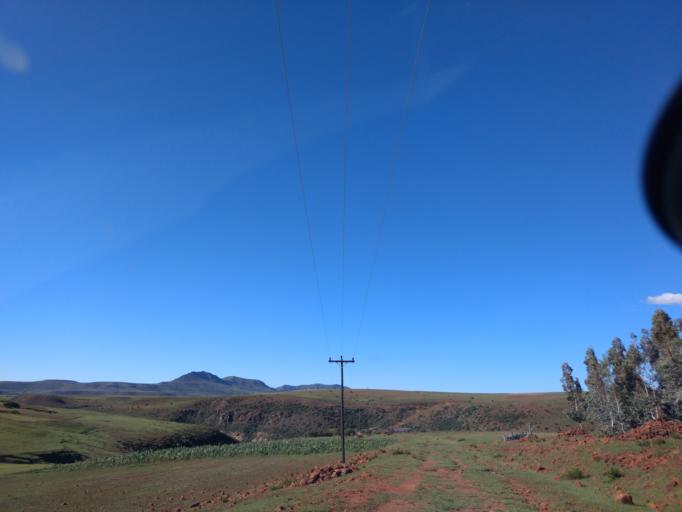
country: LS
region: Berea
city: Teyateyaneng
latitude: -29.3655
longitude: 27.7864
